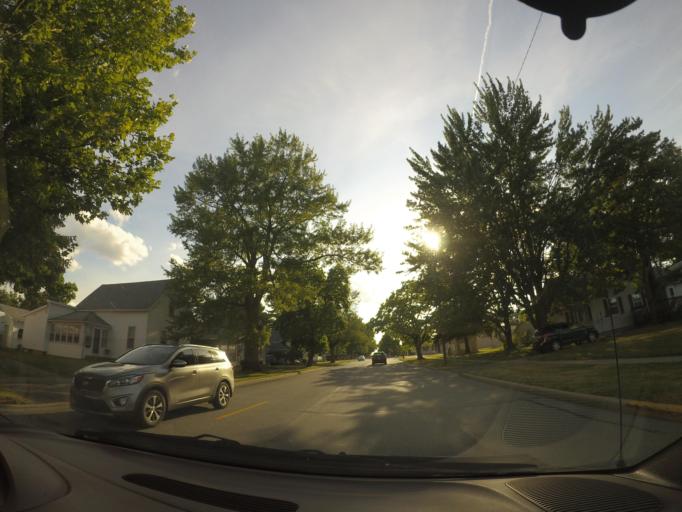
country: US
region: Indiana
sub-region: DeKalb County
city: Butler
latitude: 41.4296
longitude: -84.8794
